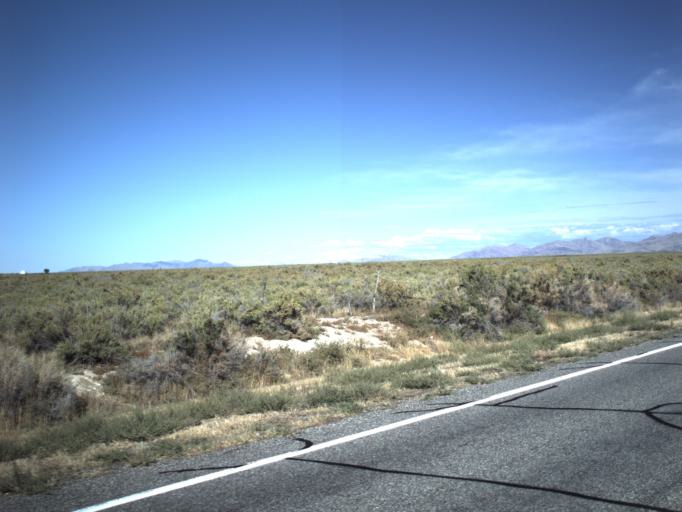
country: US
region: Utah
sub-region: Millard County
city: Delta
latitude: 39.3530
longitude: -112.5214
